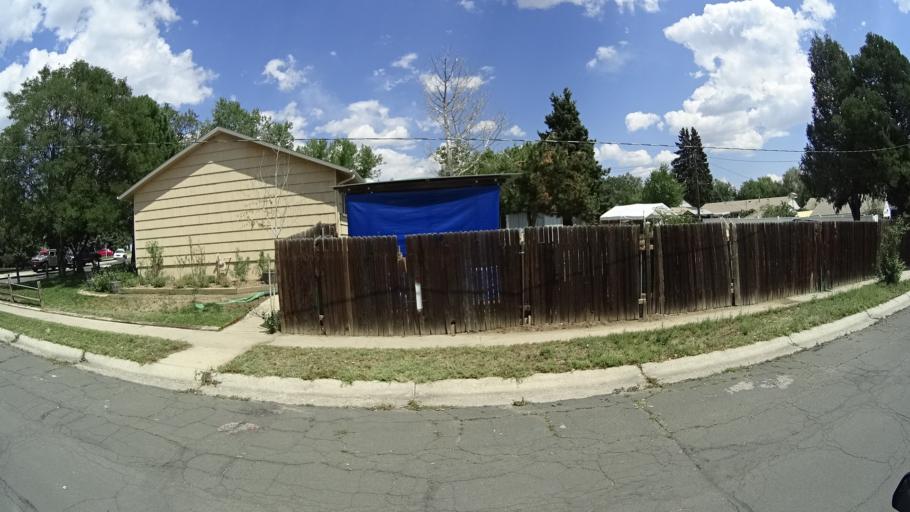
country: US
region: Colorado
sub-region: El Paso County
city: Colorado Springs
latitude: 38.8341
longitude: -104.7804
